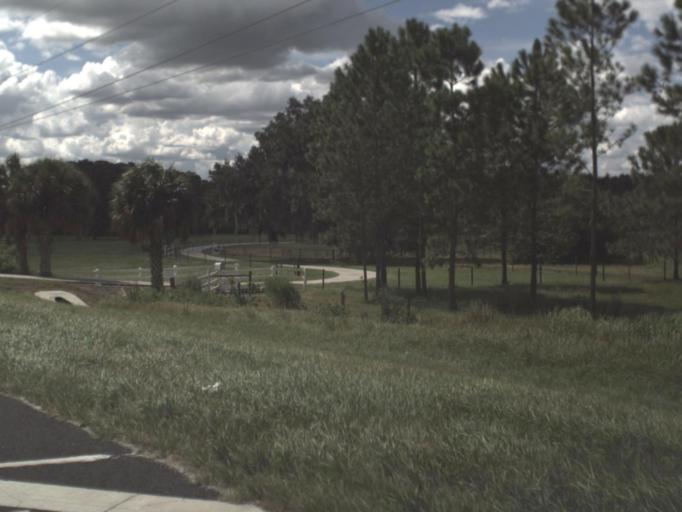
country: US
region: Florida
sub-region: Polk County
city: Bartow
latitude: 27.9038
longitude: -81.8124
